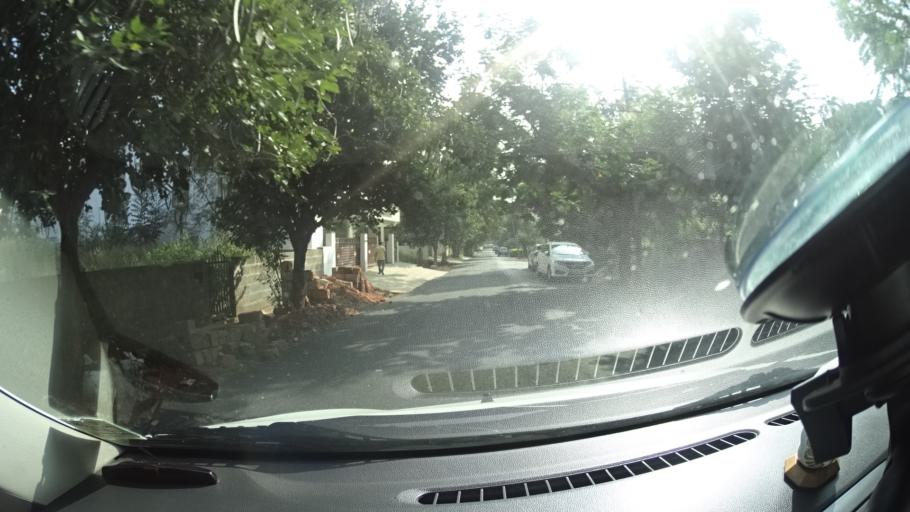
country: IN
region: Karnataka
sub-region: Bangalore Urban
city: Yelahanka
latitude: 13.0786
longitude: 77.5878
